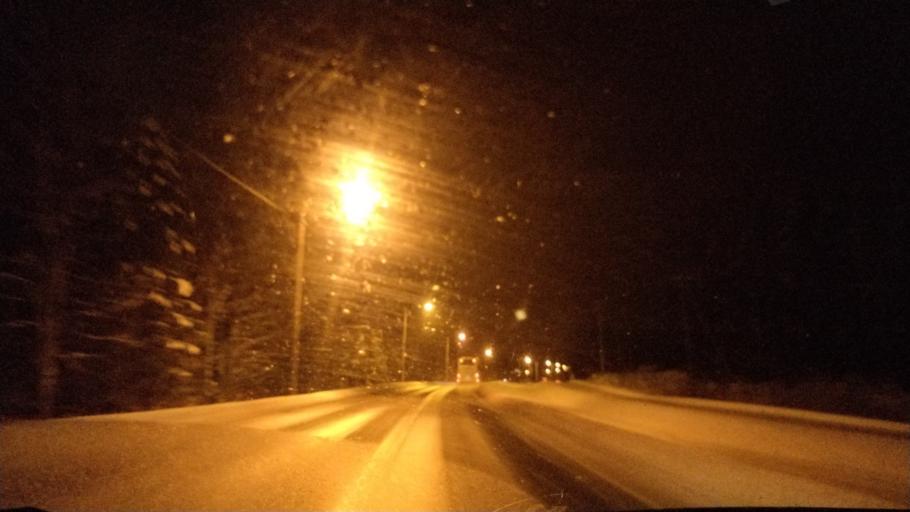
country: FI
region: Lapland
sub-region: Rovaniemi
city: Rovaniemi
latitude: 66.2895
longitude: 25.3483
